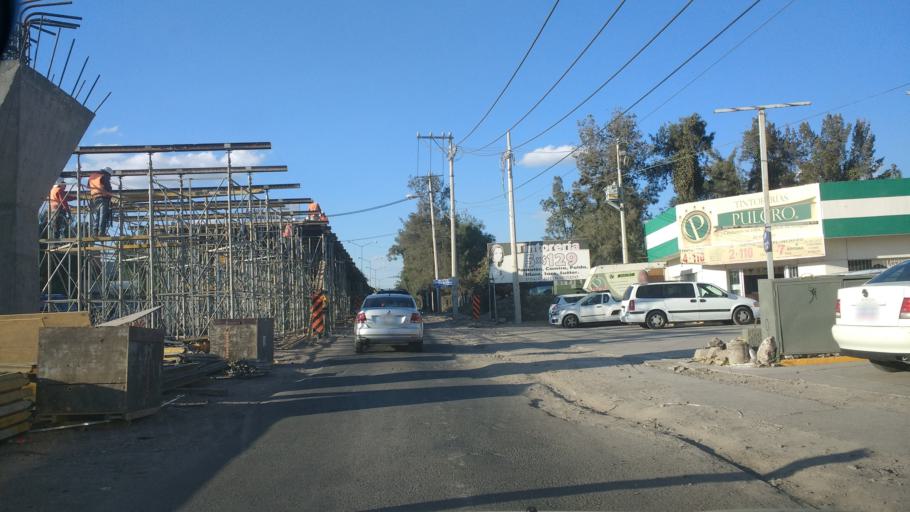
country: MX
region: Guanajuato
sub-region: Leon
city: La Ermita
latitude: 21.1706
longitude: -101.6980
